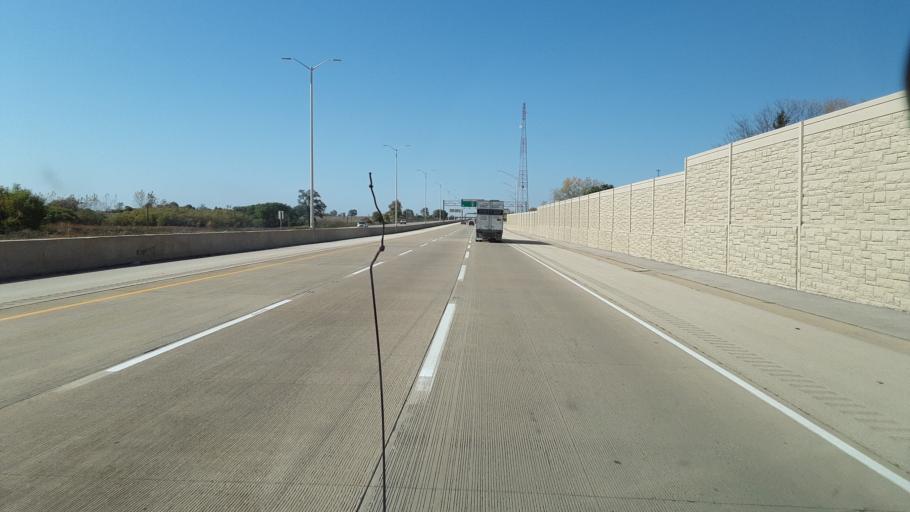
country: US
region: Illinois
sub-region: Boone County
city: Belvidere
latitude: 42.2329
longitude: -88.8452
